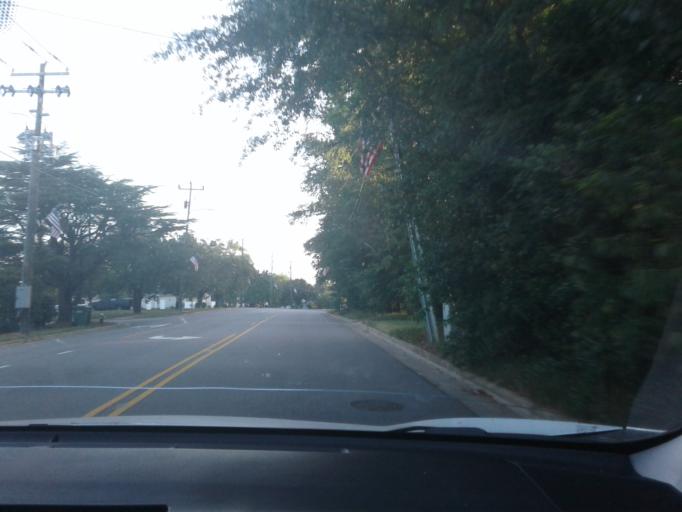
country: US
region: North Carolina
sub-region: Wake County
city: Fuquay-Varina
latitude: 35.5737
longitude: -78.8007
